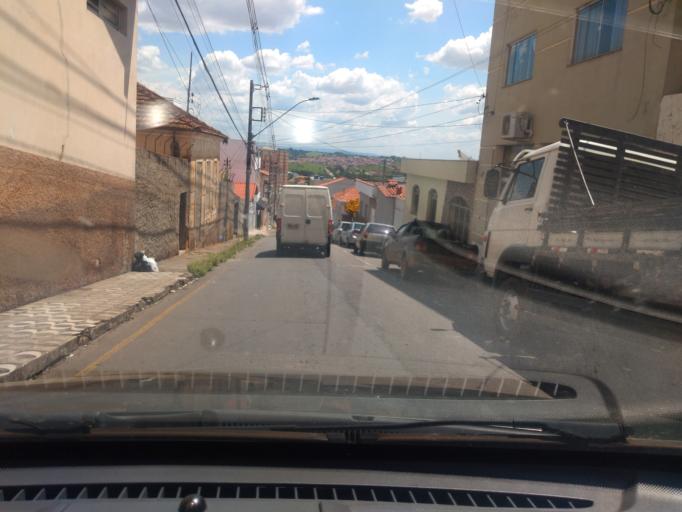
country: BR
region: Minas Gerais
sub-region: Tres Coracoes
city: Tres Coracoes
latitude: -21.6958
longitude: -45.2519
